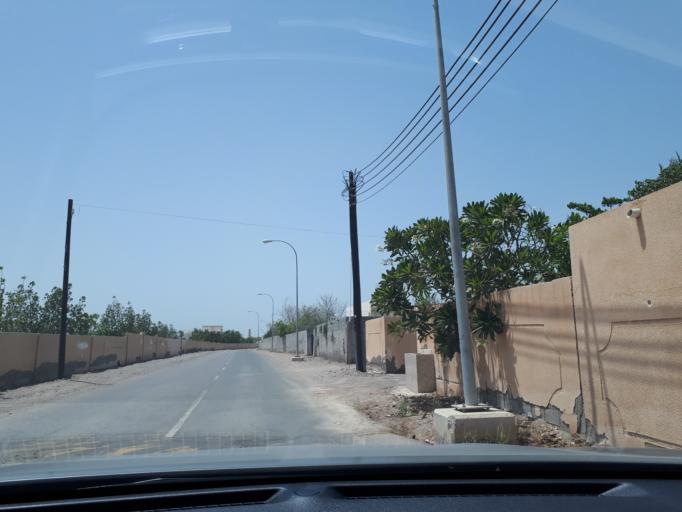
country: OM
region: Muhafazat Masqat
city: As Sib al Jadidah
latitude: 23.6847
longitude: 58.1184
